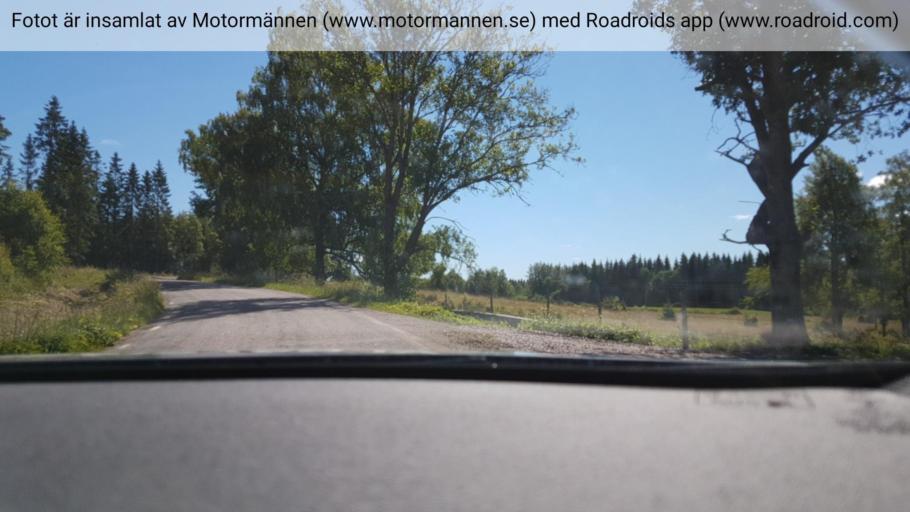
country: SE
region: Vaestra Goetaland
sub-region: Falkopings Kommun
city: Akarp
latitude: 58.1873
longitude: 13.7662
